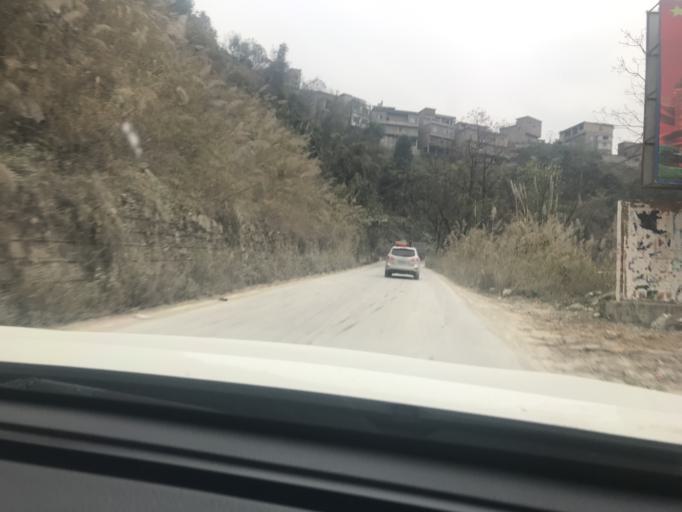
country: CN
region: Guangxi Zhuangzu Zizhiqu
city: Xinzhou
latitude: 24.9871
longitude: 105.8237
